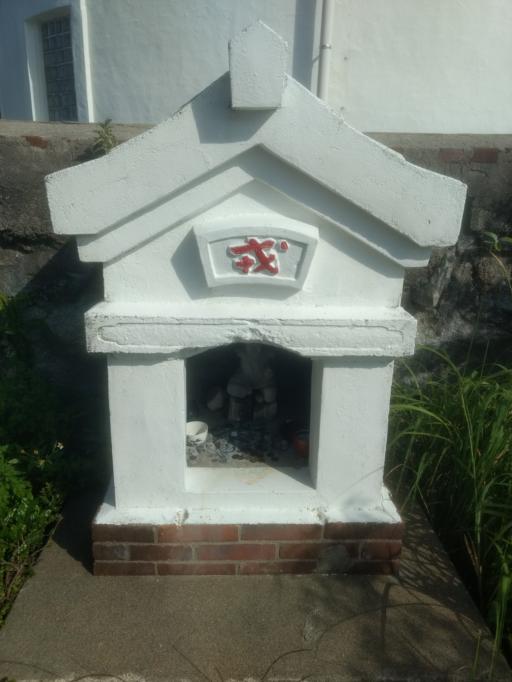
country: JP
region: Kagoshima
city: Nishinoomote
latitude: 30.3924
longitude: 130.3794
